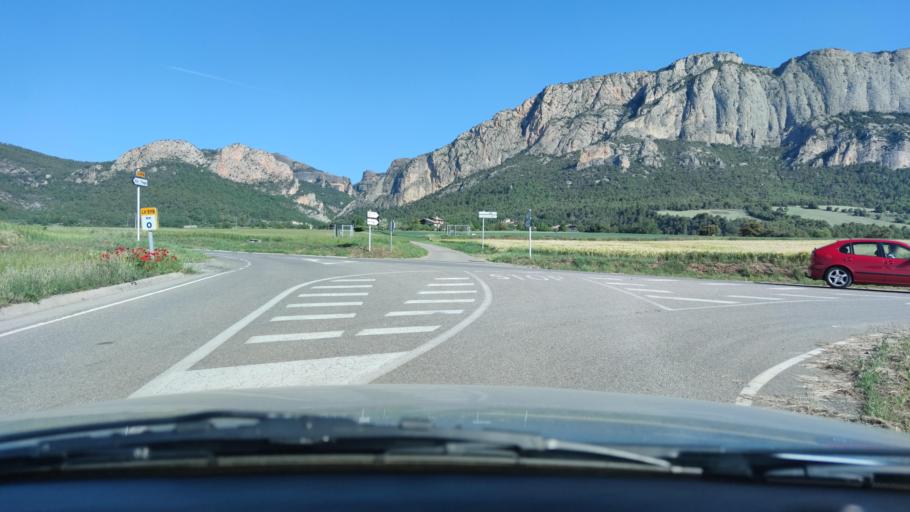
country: ES
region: Catalonia
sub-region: Provincia de Lleida
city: Oliana
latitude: 42.0651
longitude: 1.2894
